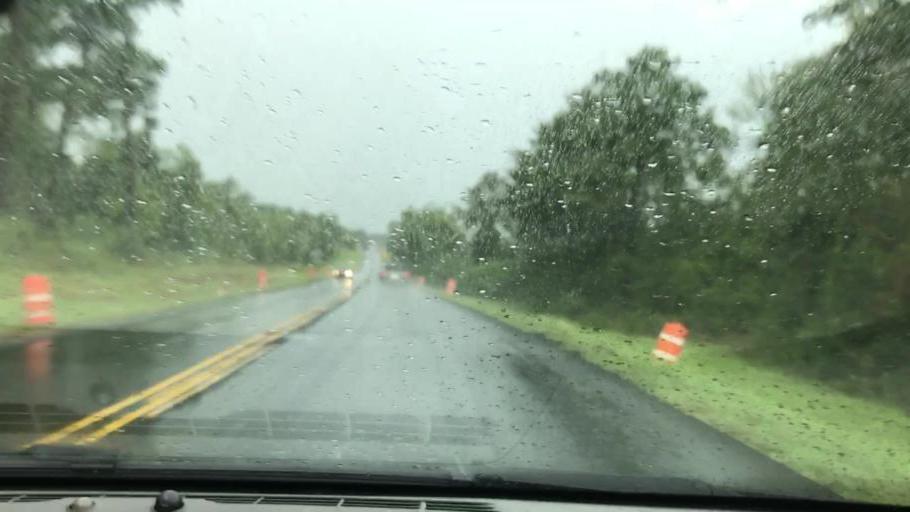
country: US
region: Georgia
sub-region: Clay County
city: Fort Gaines
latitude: 31.5752
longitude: -85.0195
